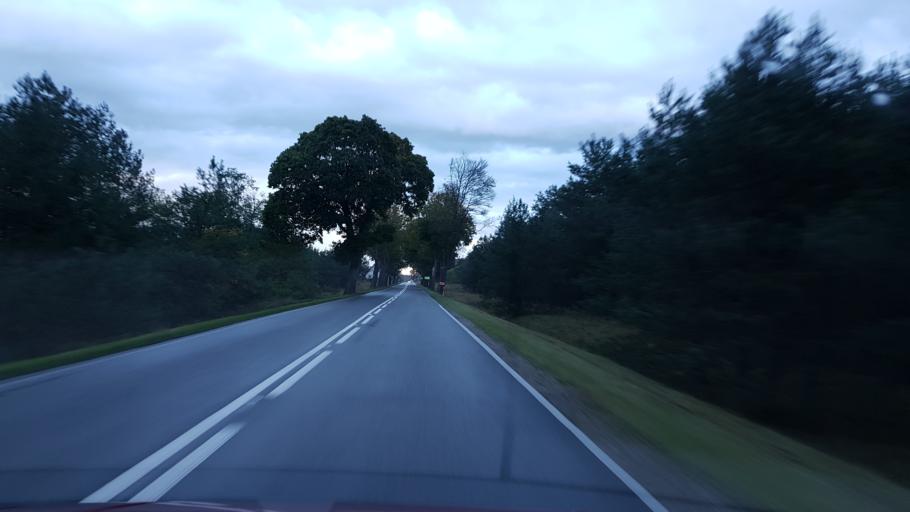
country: PL
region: Greater Poland Voivodeship
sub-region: Powiat pilski
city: Smilowo
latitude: 53.2156
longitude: 16.8634
